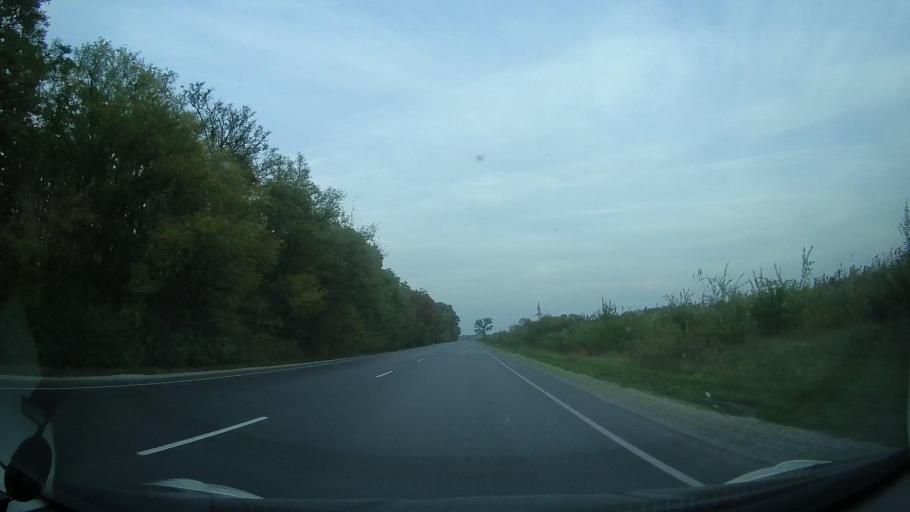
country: RU
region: Rostov
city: Ol'ginskaya
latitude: 47.1312
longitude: 39.9495
